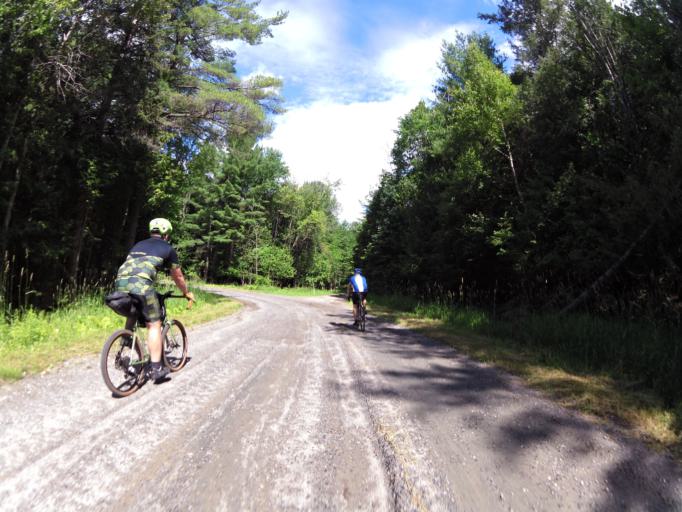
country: CA
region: Ontario
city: Perth
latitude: 45.0773
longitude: -76.4636
